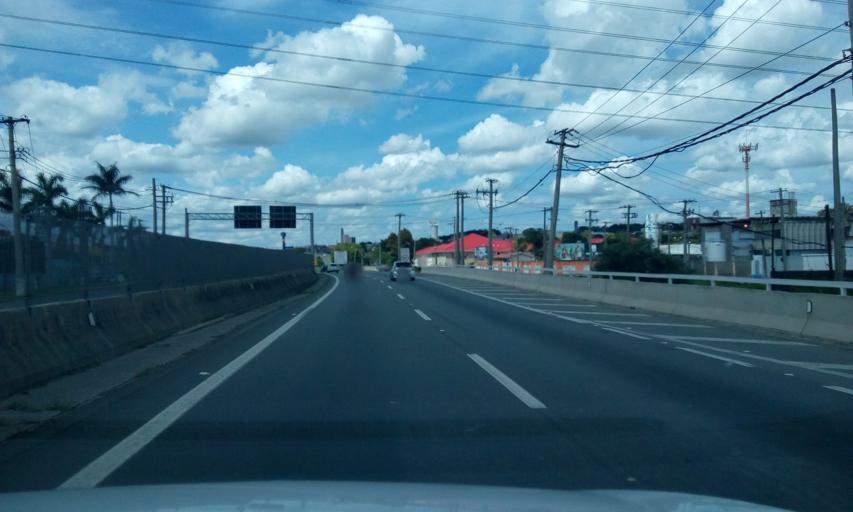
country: BR
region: Sao Paulo
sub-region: Jundiai
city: Jundiai
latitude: -23.1680
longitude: -46.9167
